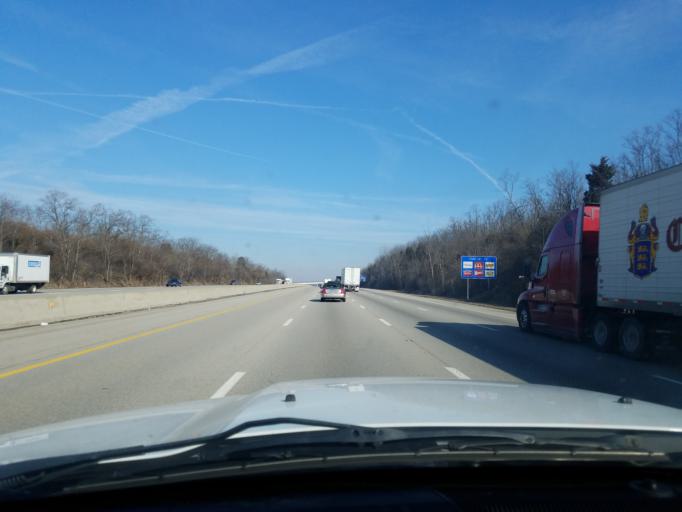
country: US
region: Ohio
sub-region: Warren County
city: Hunter
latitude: 39.4750
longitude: -84.3255
